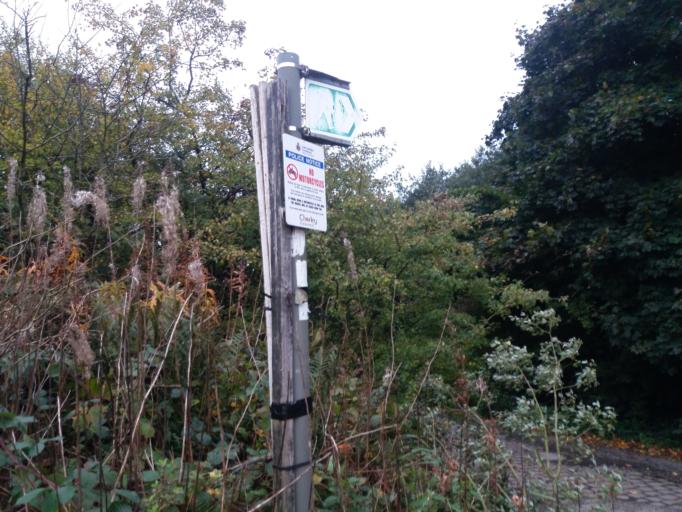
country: GB
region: England
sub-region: Lancashire
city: Chorley
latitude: 53.6652
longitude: -2.6157
